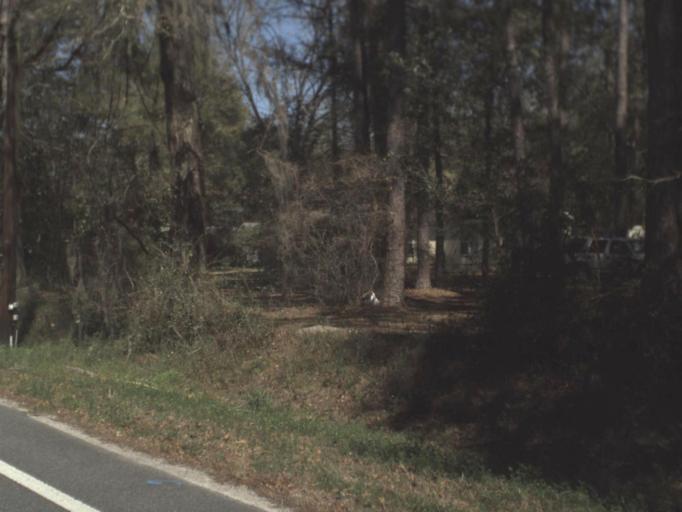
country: US
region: Florida
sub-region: Leon County
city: Woodville
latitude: 30.3074
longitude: -84.2460
